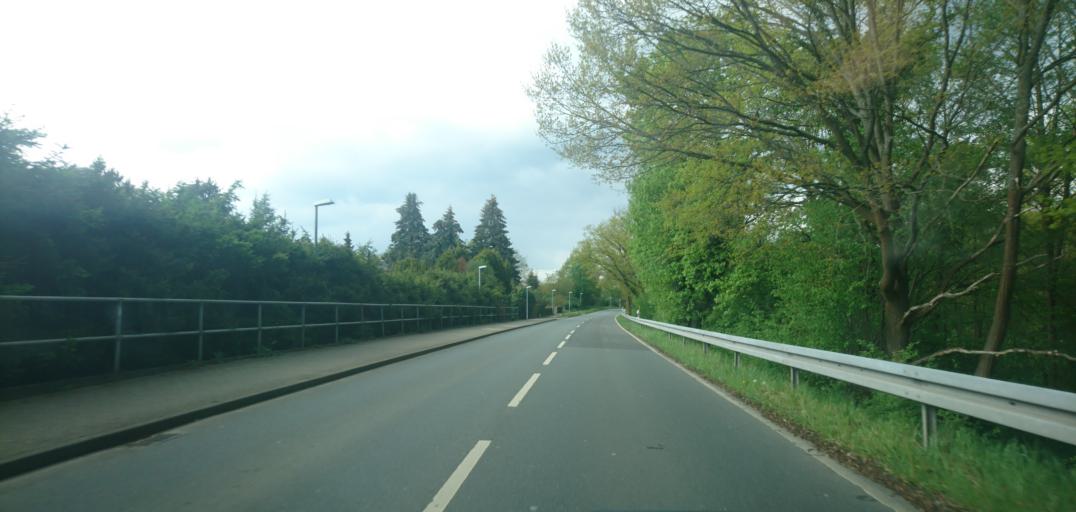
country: DE
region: Hesse
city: Dreieich
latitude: 49.9958
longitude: 8.7254
